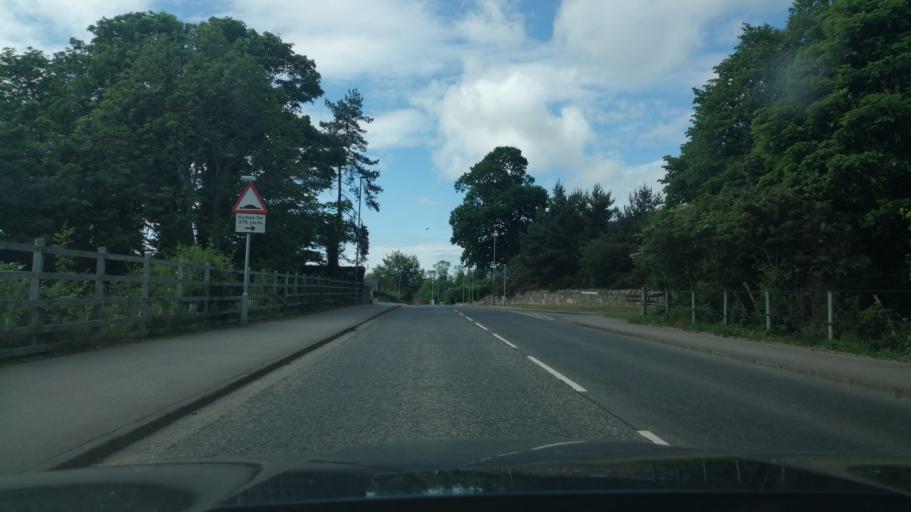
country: GB
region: Scotland
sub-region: Moray
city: Elgin
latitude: 57.6560
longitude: -3.3023
